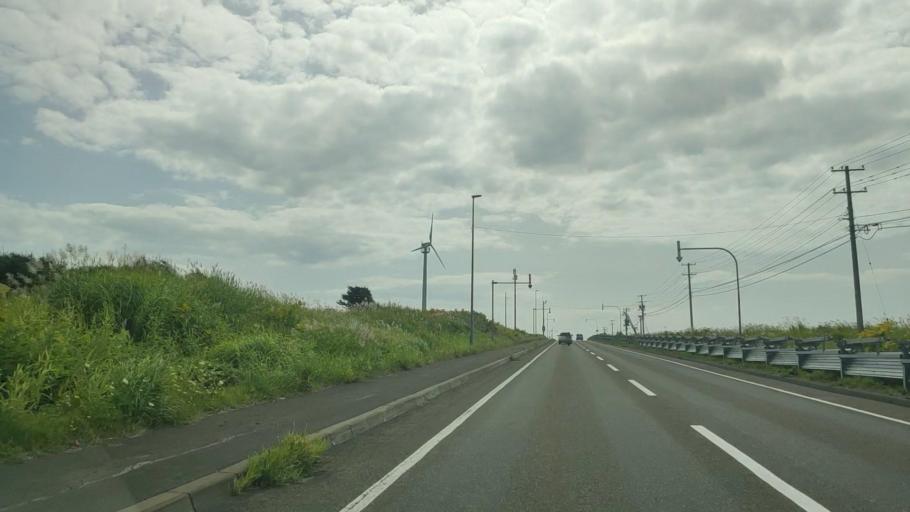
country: JP
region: Hokkaido
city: Rumoi
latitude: 44.4089
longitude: 141.7321
